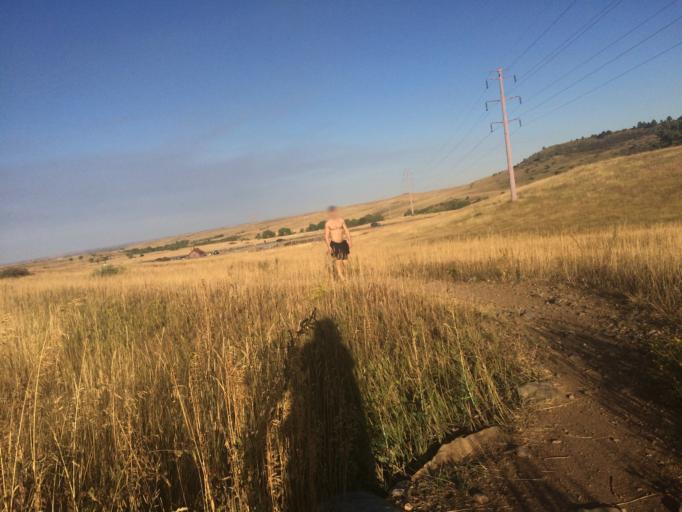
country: US
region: Colorado
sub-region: Boulder County
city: Superior
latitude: 39.9237
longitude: -105.2388
